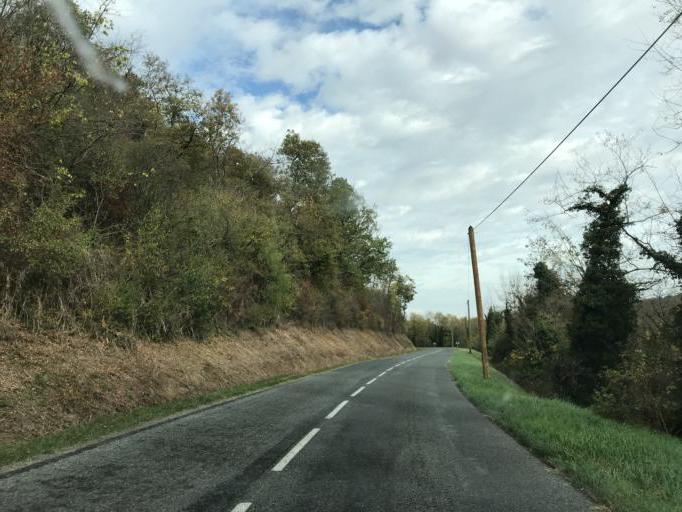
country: FR
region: Rhone-Alpes
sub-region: Departement de l'Ain
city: Dagneux
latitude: 45.8600
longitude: 5.0713
